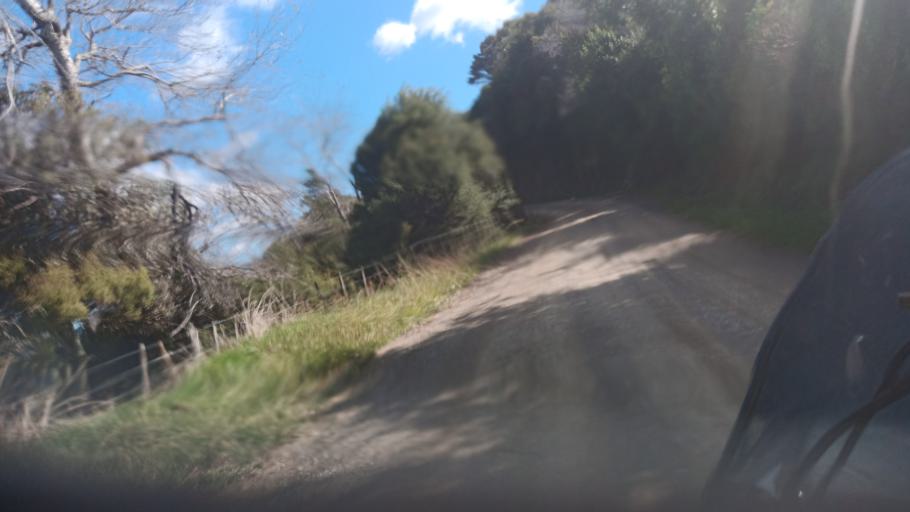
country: NZ
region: Gisborne
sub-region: Gisborne District
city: Gisborne
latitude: -38.3965
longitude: 177.6745
